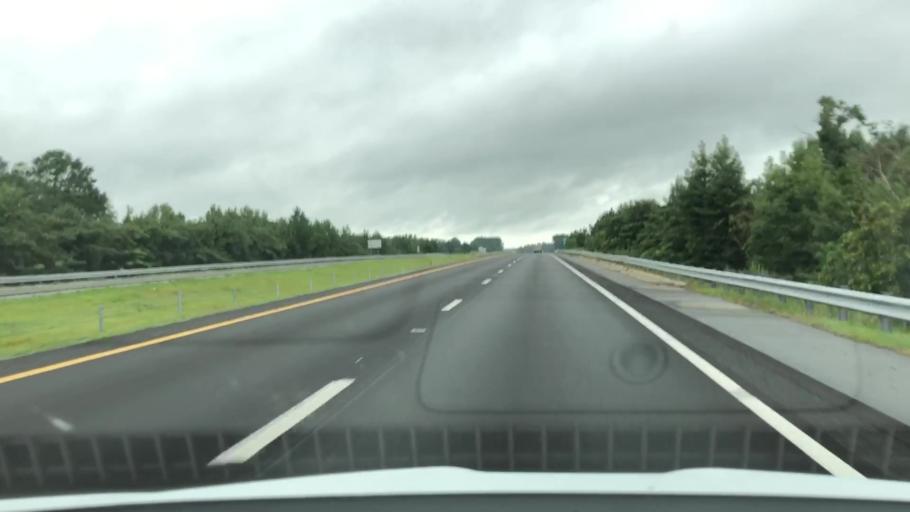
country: US
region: North Carolina
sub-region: Wayne County
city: Goldsboro
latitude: 35.4403
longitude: -77.9843
